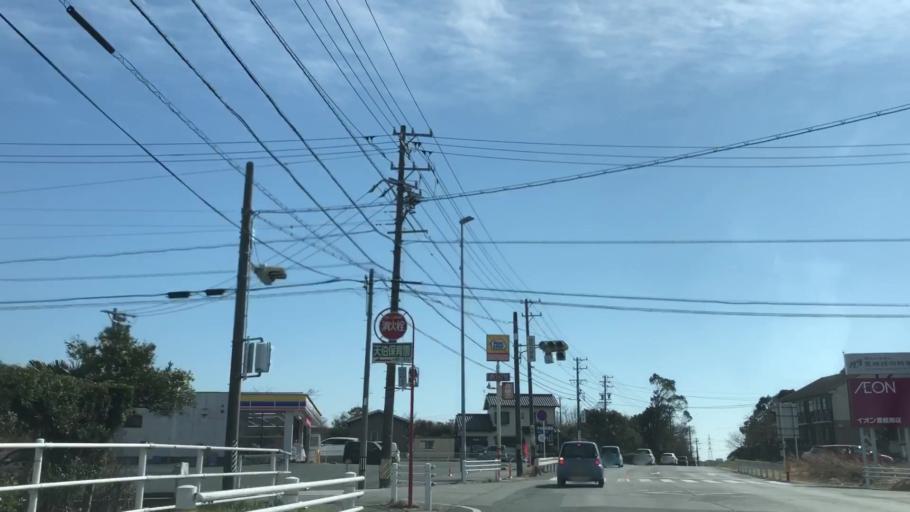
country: JP
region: Aichi
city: Toyohashi
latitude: 34.7013
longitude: 137.4143
